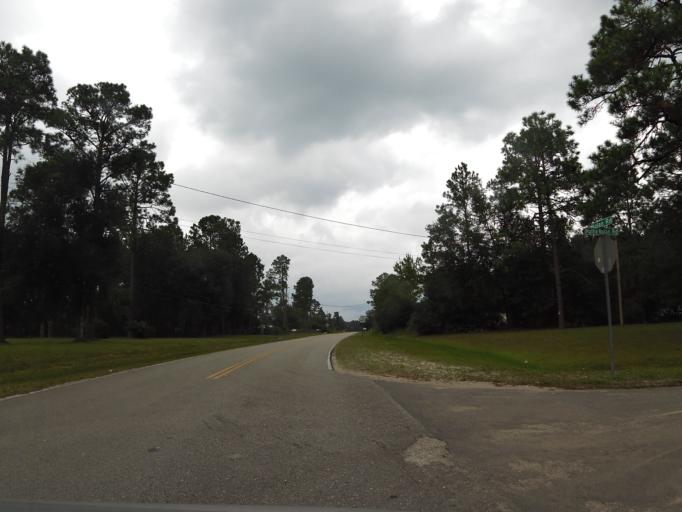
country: US
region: Florida
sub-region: Clay County
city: Middleburg
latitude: 30.1204
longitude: -81.9492
